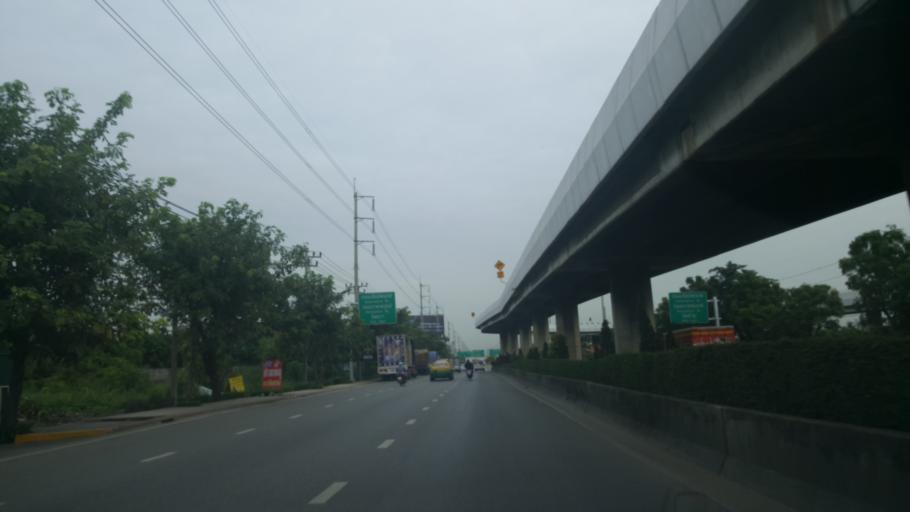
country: TH
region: Bangkok
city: Bang Bon
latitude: 13.6739
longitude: 100.4060
